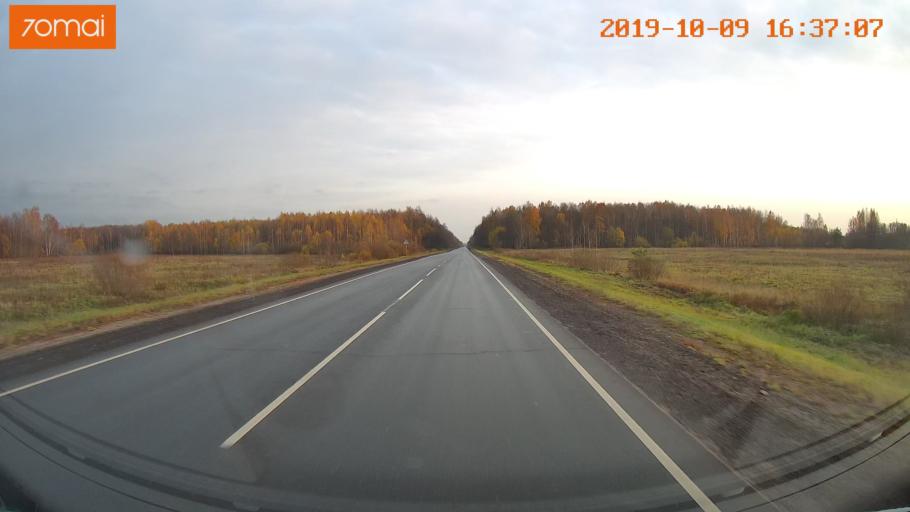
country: RU
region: Kostroma
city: Volgorechensk
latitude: 57.5316
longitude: 41.0208
